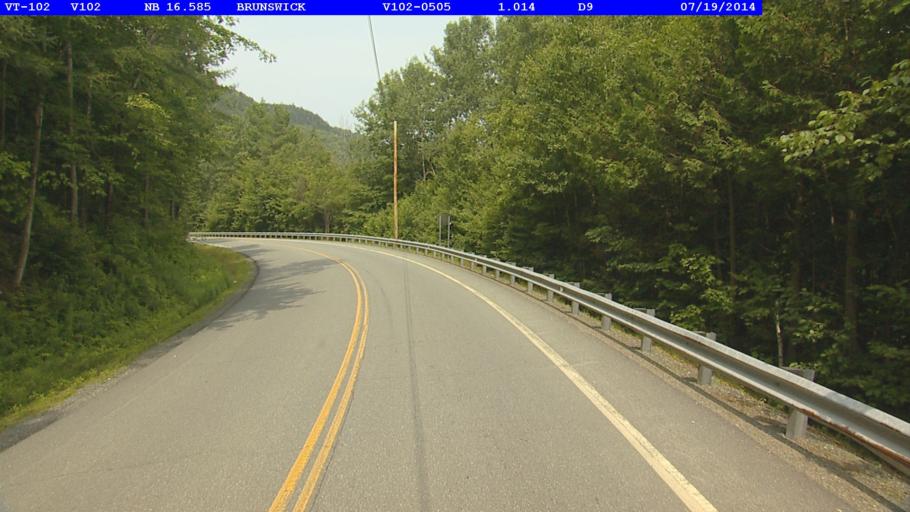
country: US
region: New Hampshire
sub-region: Coos County
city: Stratford
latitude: 44.6760
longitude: -71.5939
